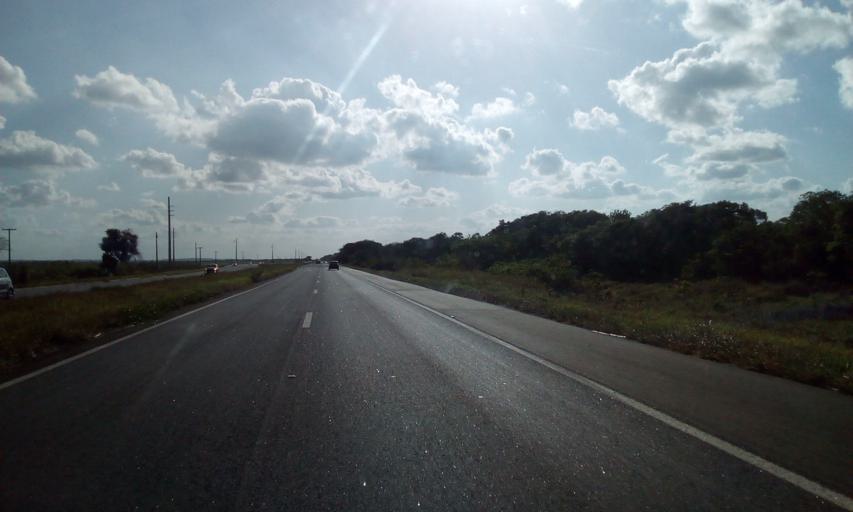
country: BR
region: Paraiba
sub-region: Santa Rita
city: Santa Rita
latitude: -7.1618
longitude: -35.0226
